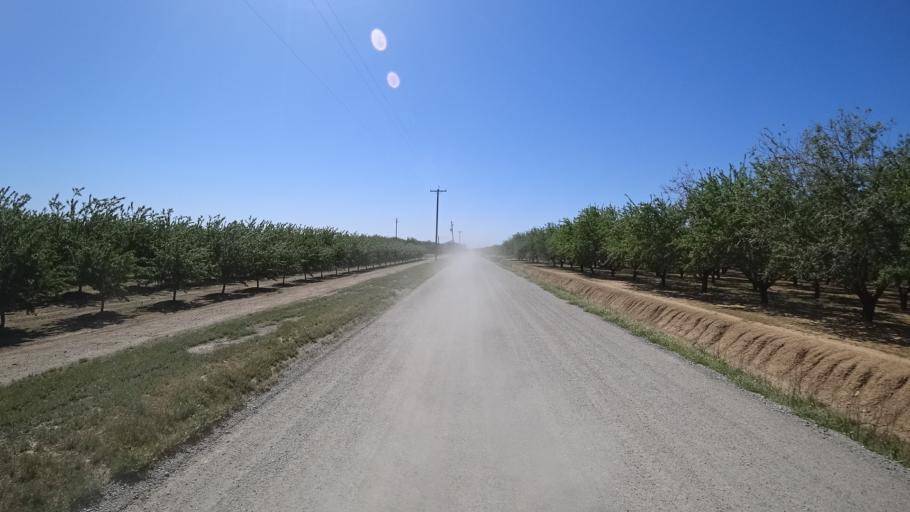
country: US
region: California
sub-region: Glenn County
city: Orland
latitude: 39.6938
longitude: -122.1591
